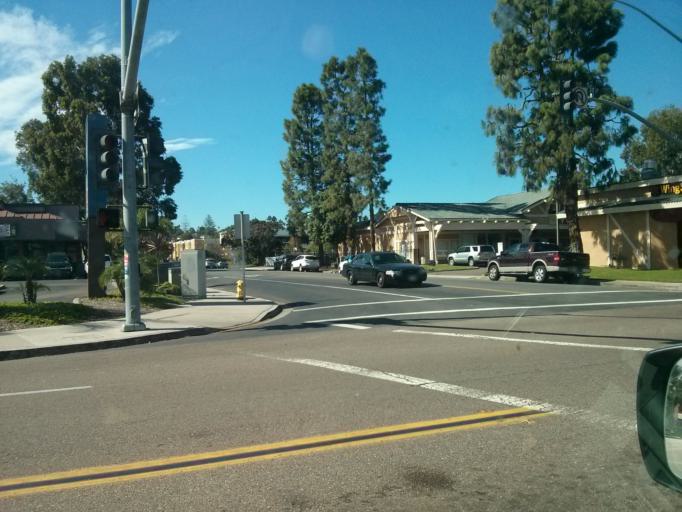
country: US
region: California
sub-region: San Diego County
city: San Diego
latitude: 32.7510
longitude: -117.2134
